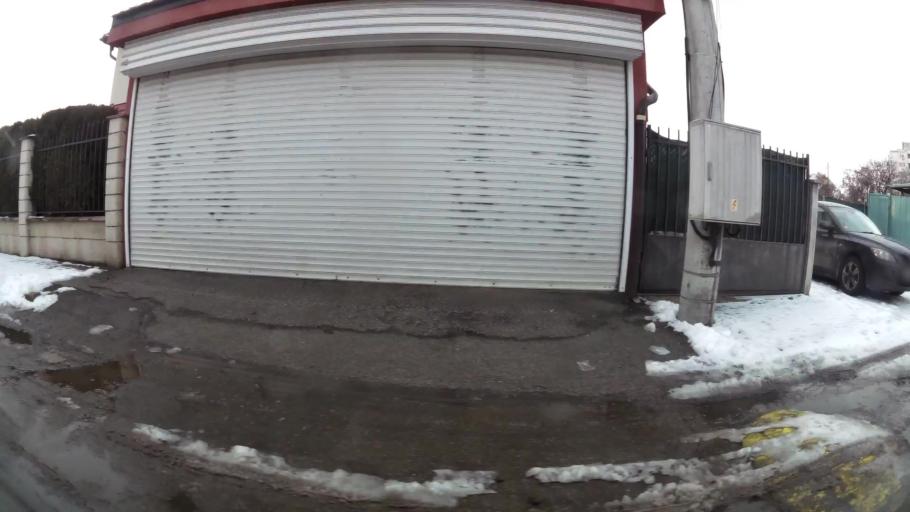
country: BG
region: Sofia-Capital
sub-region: Stolichna Obshtina
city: Sofia
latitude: 42.7258
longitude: 23.3469
